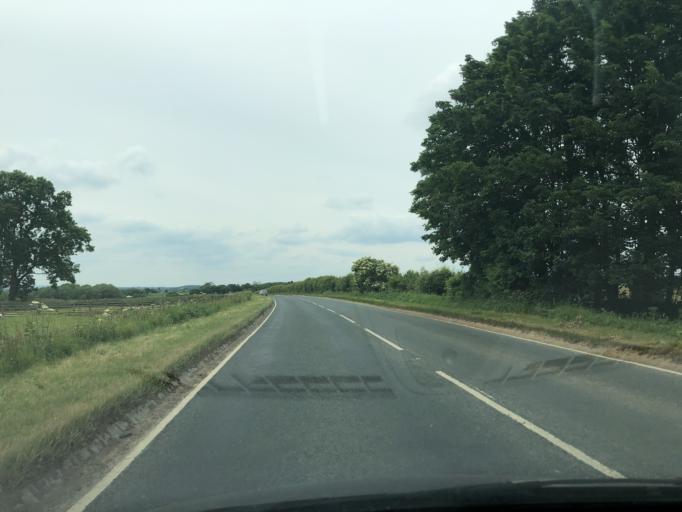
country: GB
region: England
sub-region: North Yorkshire
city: Great Habton
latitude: 54.2631
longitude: -0.8841
